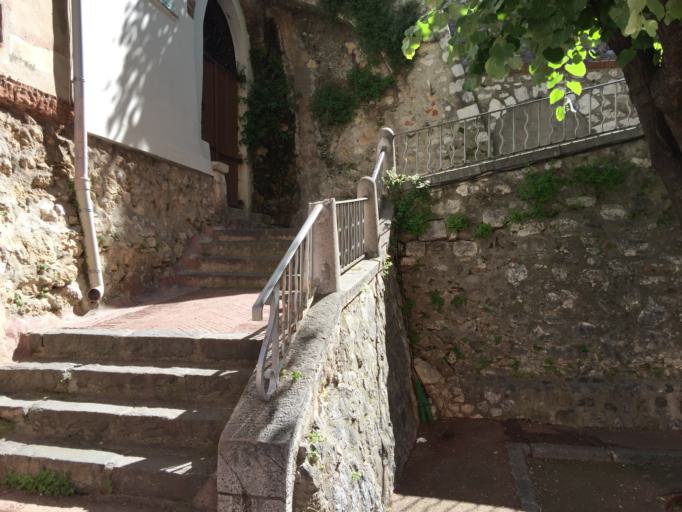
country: FR
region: Provence-Alpes-Cote d'Azur
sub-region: Departement des Alpes-Maritimes
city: Nice
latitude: 43.6983
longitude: 7.2791
